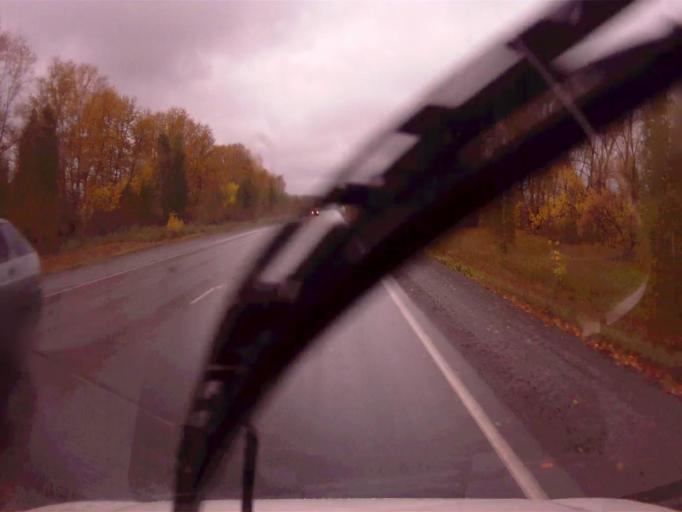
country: RU
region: Chelyabinsk
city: Argayash
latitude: 55.4527
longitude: 60.9334
